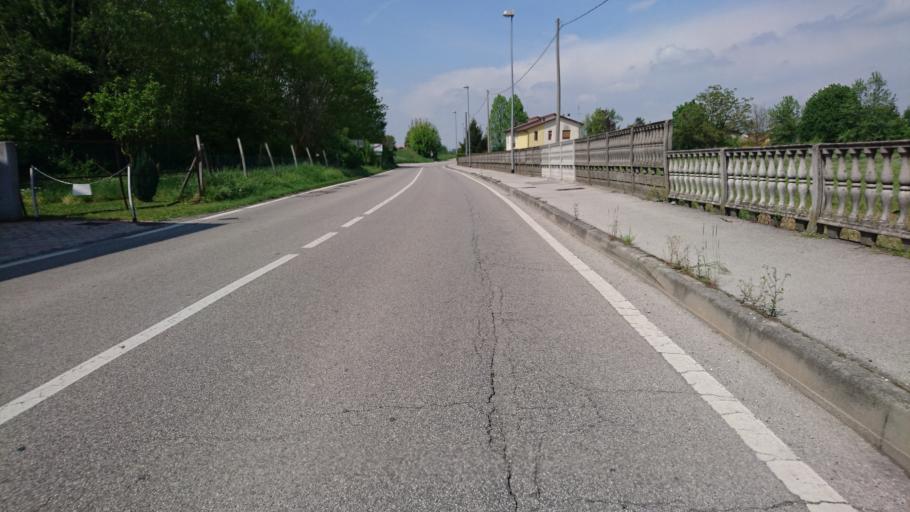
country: IT
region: Veneto
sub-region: Provincia di Padova
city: Saletto
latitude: 45.4793
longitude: 11.8553
